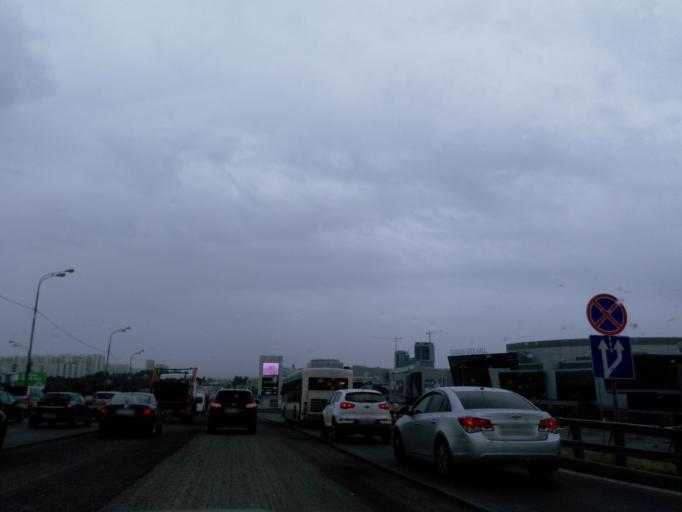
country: RU
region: Moscow
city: Strogino
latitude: 55.8275
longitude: 37.3941
